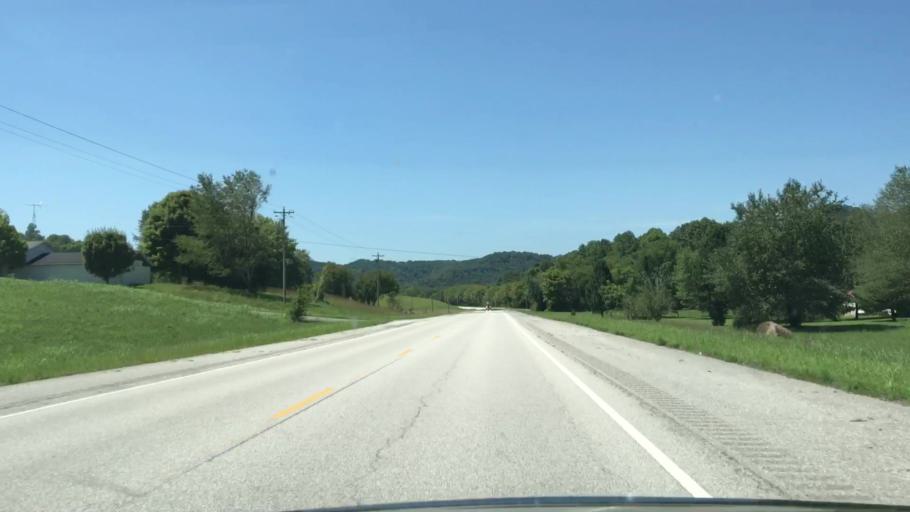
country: US
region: Tennessee
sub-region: Jackson County
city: Gainesboro
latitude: 36.4364
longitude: -85.6219
